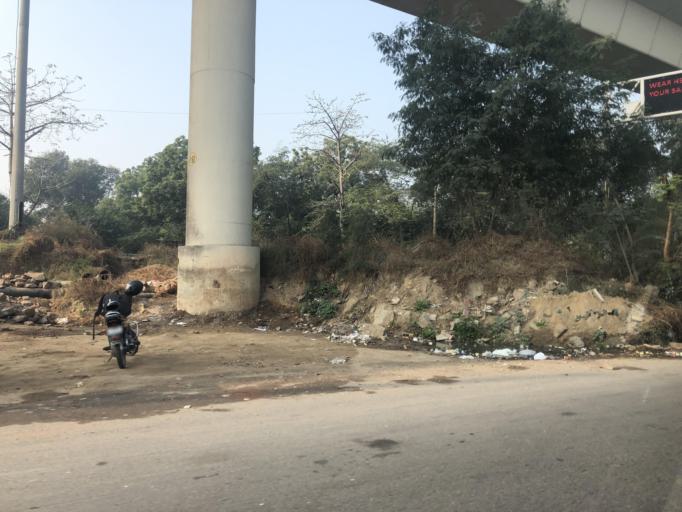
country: IN
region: NCT
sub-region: Central Delhi
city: Karol Bagh
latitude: 28.5991
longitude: 77.1627
